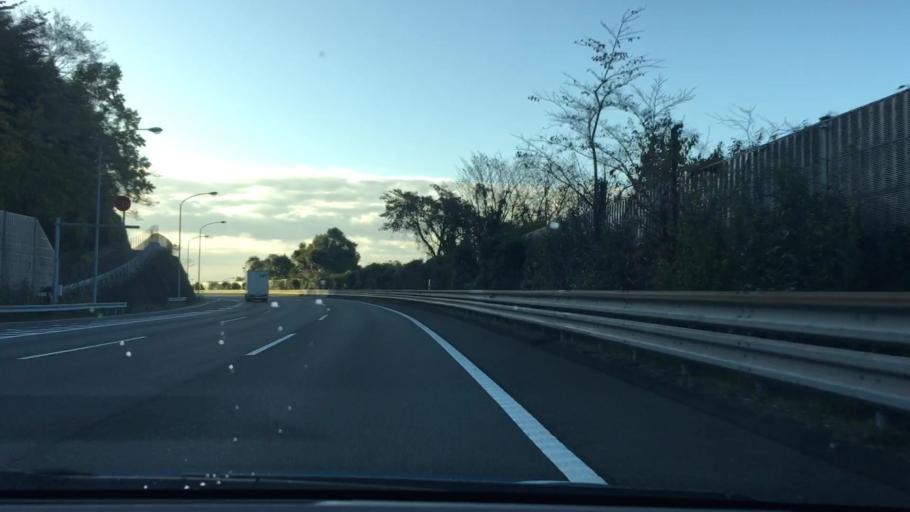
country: JP
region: Kanagawa
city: Hadano
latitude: 35.3637
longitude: 139.1023
